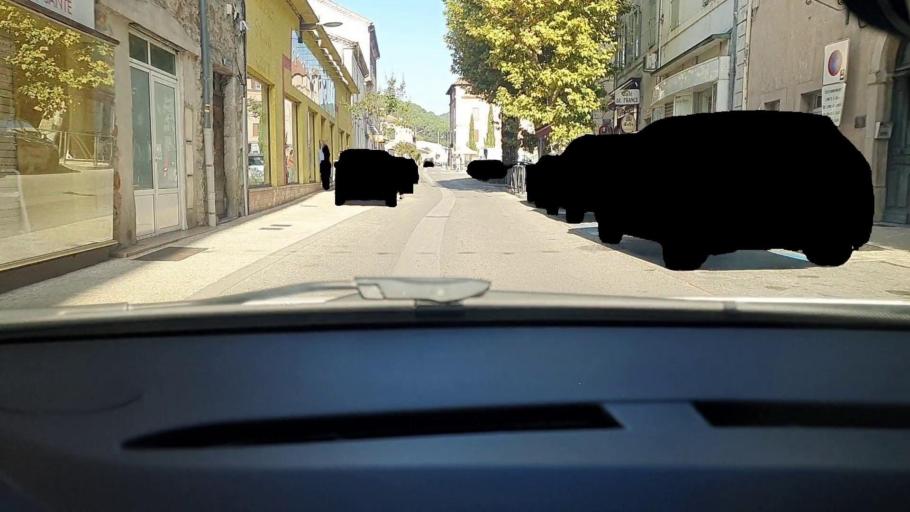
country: FR
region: Languedoc-Roussillon
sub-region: Departement du Gard
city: Besseges
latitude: 44.2917
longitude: 4.0970
